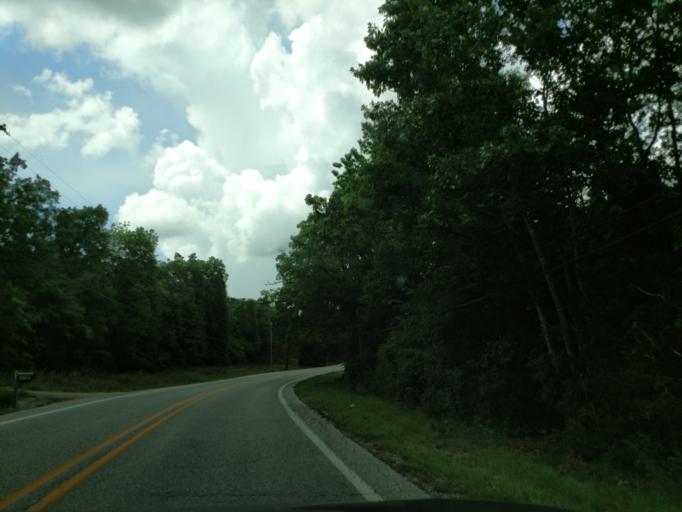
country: US
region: Arkansas
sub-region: Boone County
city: Harrison
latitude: 36.2391
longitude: -93.2117
